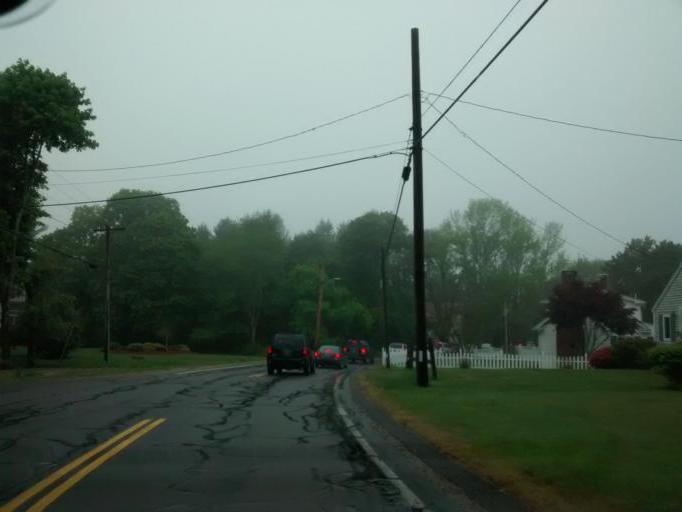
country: US
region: Massachusetts
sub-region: Barnstable County
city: Pocasset
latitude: 41.6929
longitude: -70.6050
